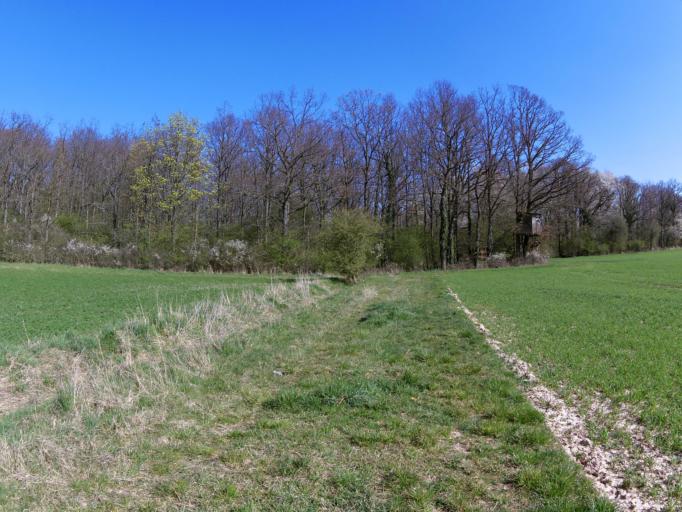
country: DE
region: Bavaria
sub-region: Regierungsbezirk Unterfranken
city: Kurnach
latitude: 49.8296
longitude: 10.0541
